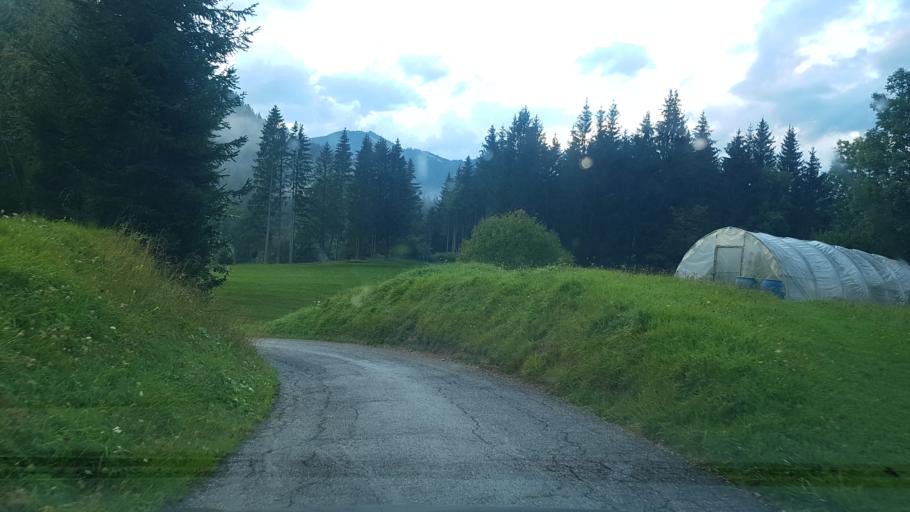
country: IT
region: Friuli Venezia Giulia
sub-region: Provincia di Udine
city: Tarvisio
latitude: 46.4865
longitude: 13.6173
